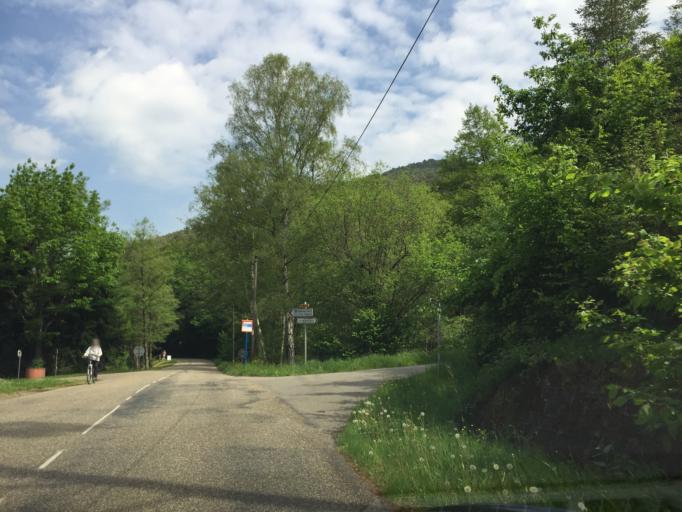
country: DE
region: Rheinland-Pfalz
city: Hirschthal
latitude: 49.0311
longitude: 7.7692
